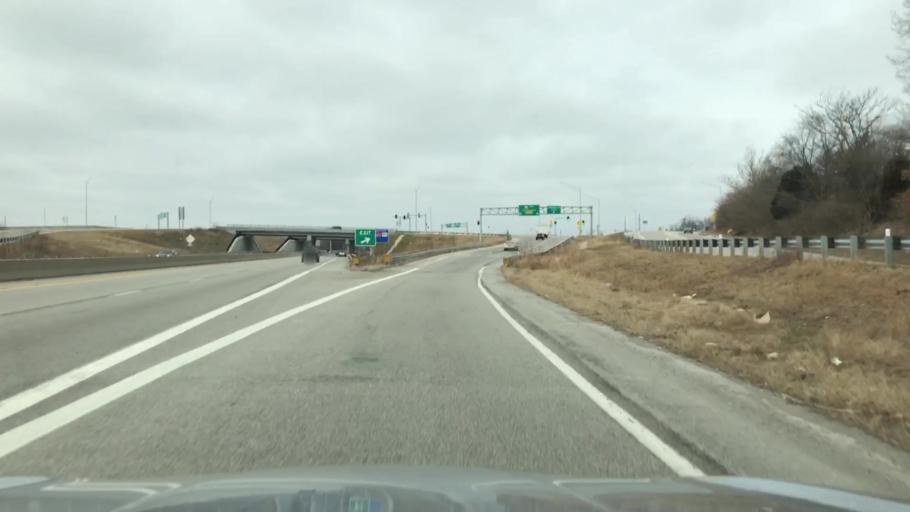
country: US
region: Missouri
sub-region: Jackson County
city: Lees Summit
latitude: 38.9032
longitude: -94.3739
